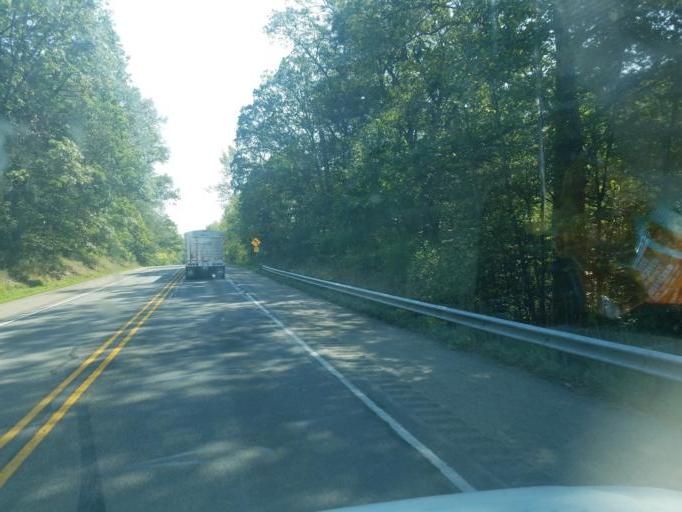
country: US
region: Indiana
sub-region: Steuben County
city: Angola
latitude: 41.6374
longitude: -85.1556
